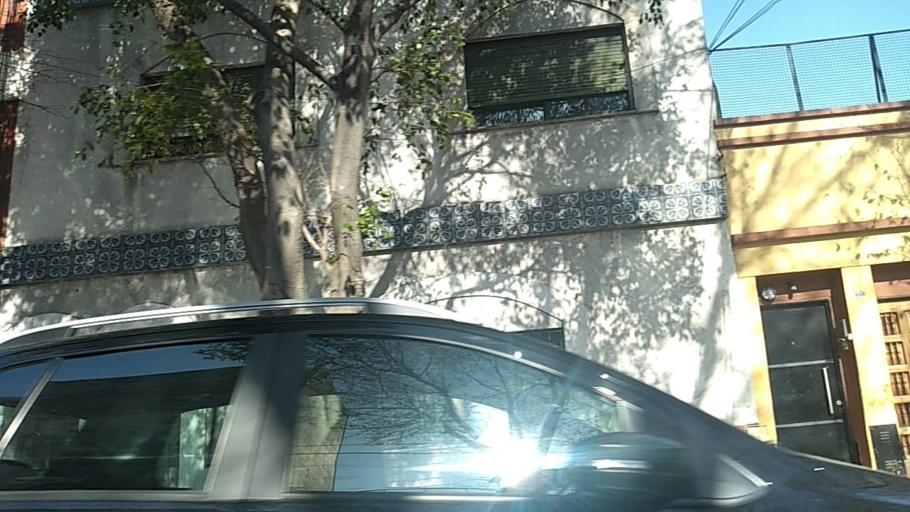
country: AR
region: Buenos Aires F.D.
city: Villa Santa Rita
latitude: -34.6057
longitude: -58.5070
